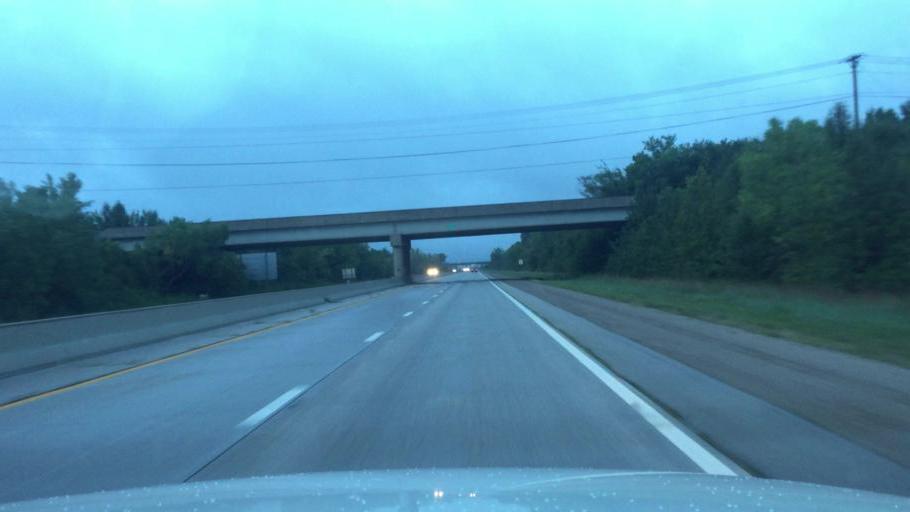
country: US
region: Kansas
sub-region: Neosho County
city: Chanute
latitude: 37.6829
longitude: -95.4796
